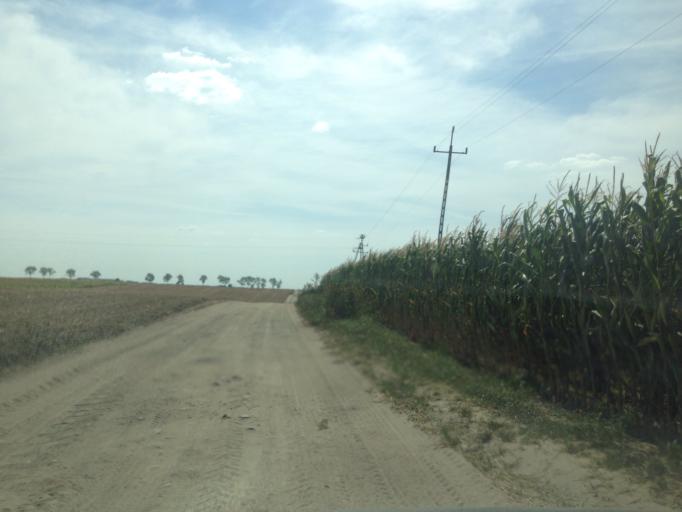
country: PL
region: Kujawsko-Pomorskie
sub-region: Powiat brodnicki
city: Gorzno
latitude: 53.2070
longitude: 19.6236
